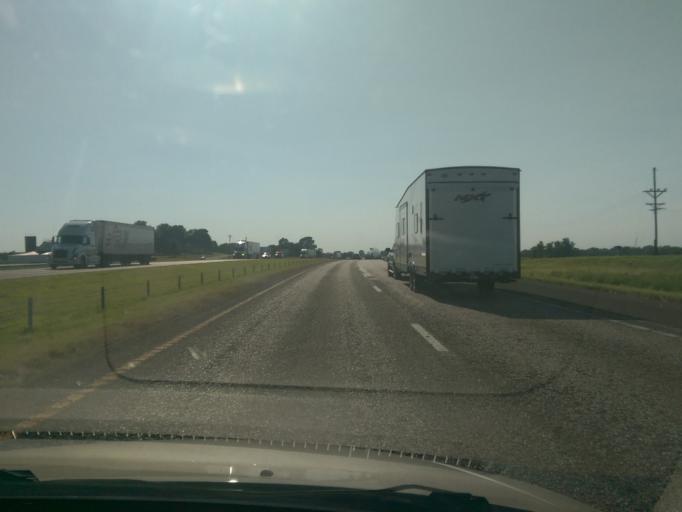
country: US
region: Missouri
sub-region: Lafayette County
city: Concordia
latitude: 38.9891
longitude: -93.5485
